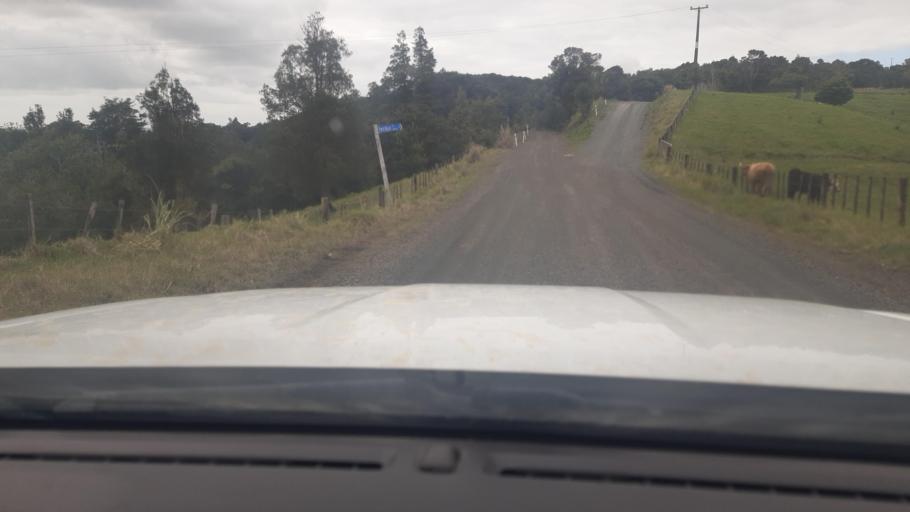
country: NZ
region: Northland
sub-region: Far North District
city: Kaitaia
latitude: -35.0714
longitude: 173.3310
